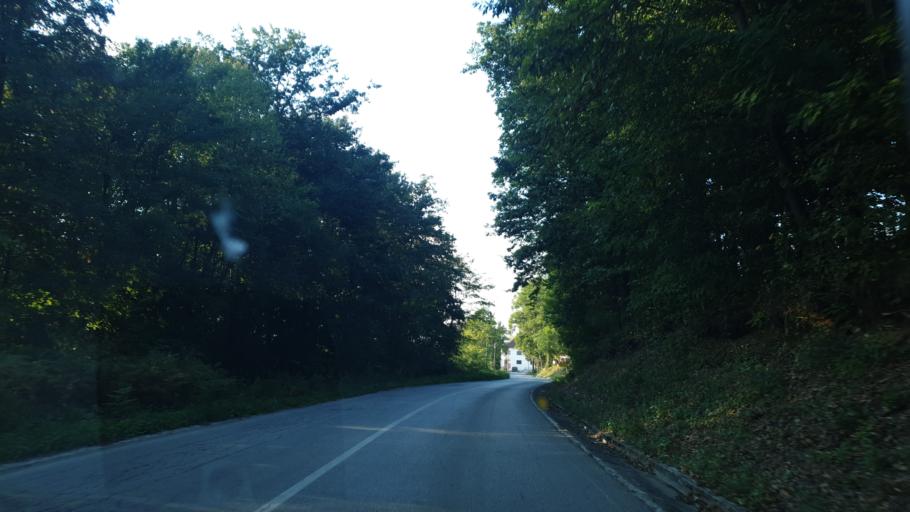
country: RS
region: Central Serbia
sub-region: Zlatiborski Okrug
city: Pozega
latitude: 43.9592
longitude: 20.0280
